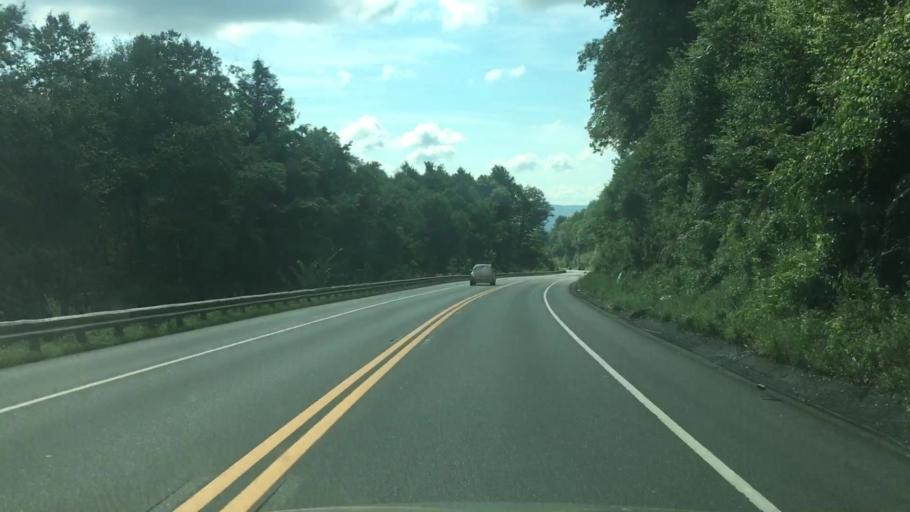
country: US
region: Massachusetts
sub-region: Franklin County
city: Greenfield
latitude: 42.6012
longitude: -72.6371
